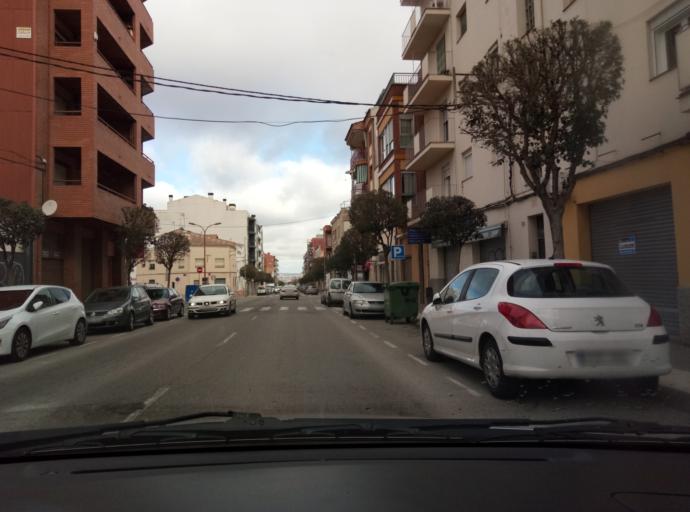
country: ES
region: Catalonia
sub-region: Provincia de Lleida
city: Tarrega
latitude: 41.6532
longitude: 1.1383
